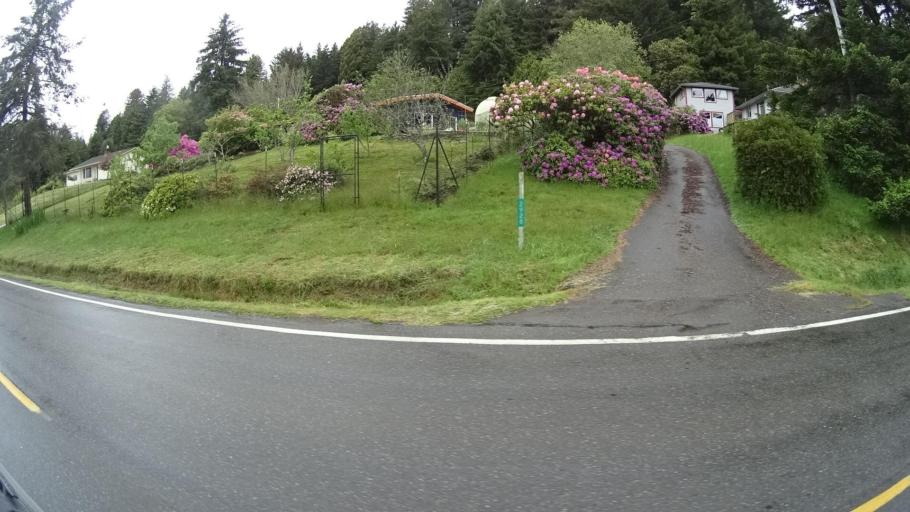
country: US
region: California
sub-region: Humboldt County
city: Bayside
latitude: 40.8389
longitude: -124.0564
